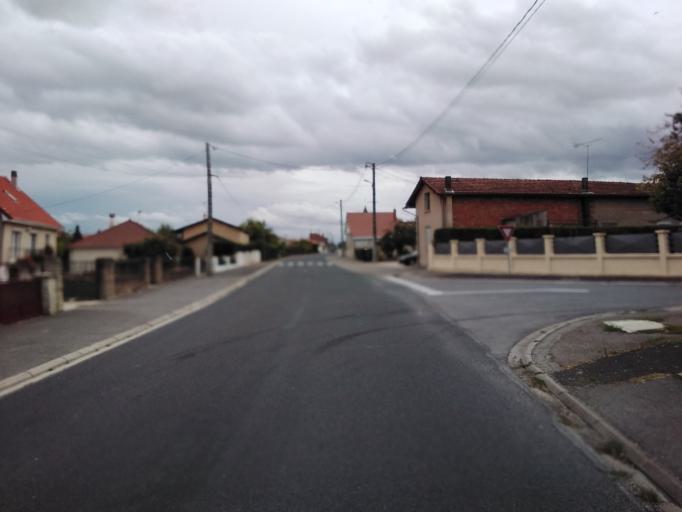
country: FR
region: Champagne-Ardenne
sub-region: Departement de la Marne
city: Frignicourt
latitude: 48.6741
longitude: 4.5819
